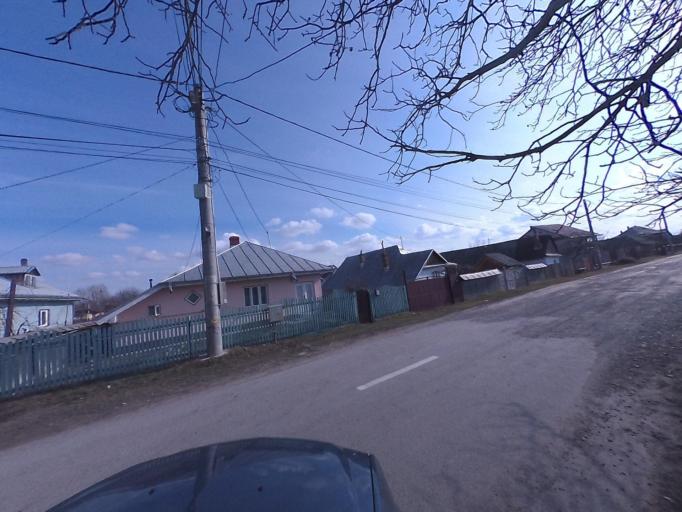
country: RO
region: Neamt
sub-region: Oras Targu Neamt
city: Targu Neamt
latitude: 47.2069
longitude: 26.3836
